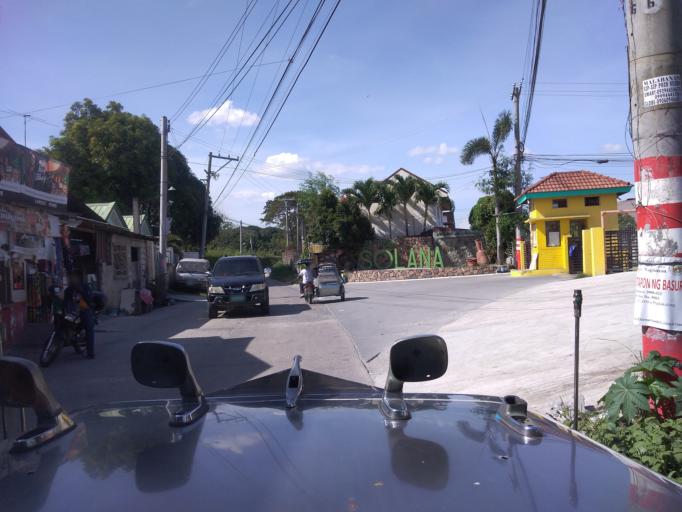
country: PH
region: Central Luzon
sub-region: Province of Pampanga
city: Magliman
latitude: 15.0384
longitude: 120.6610
